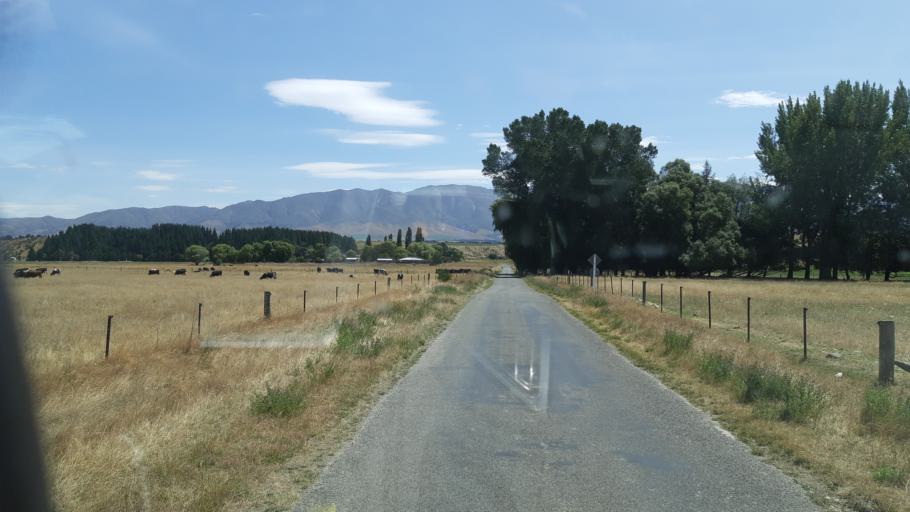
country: NZ
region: Otago
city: Oamaru
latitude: -44.6599
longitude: 170.5996
